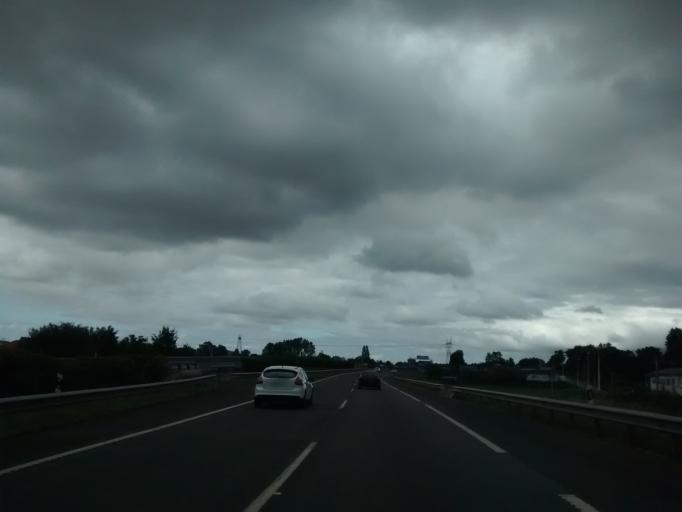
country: ES
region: Cantabria
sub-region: Provincia de Cantabria
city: Cartes
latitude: 43.3208
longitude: -4.0609
